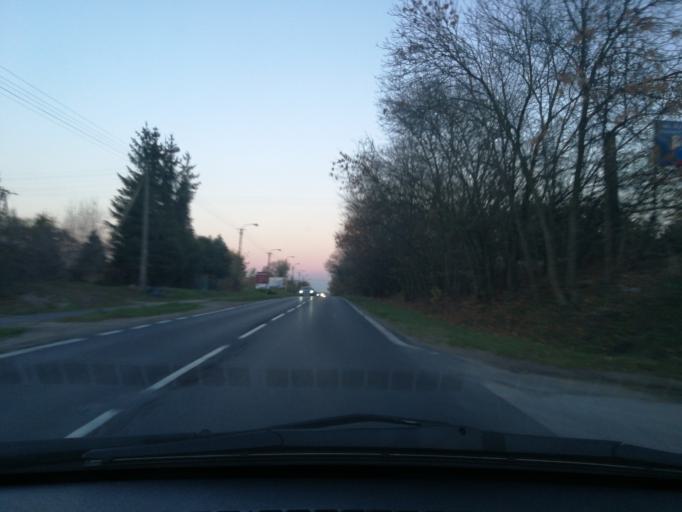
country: PL
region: Lodz Voivodeship
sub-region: Powiat lodzki wschodni
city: Andrespol
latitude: 51.7947
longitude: 19.5762
